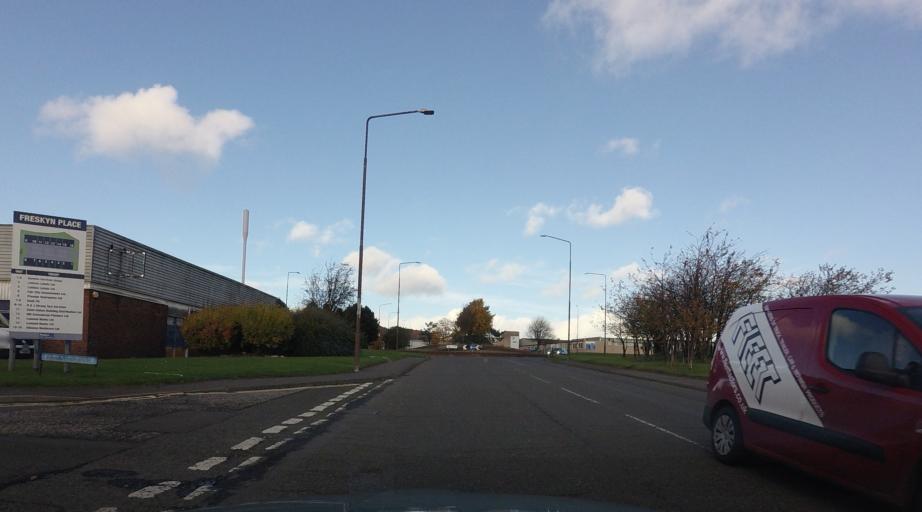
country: GB
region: Scotland
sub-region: West Lothian
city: Broxburn
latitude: 55.9375
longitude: -3.4529
